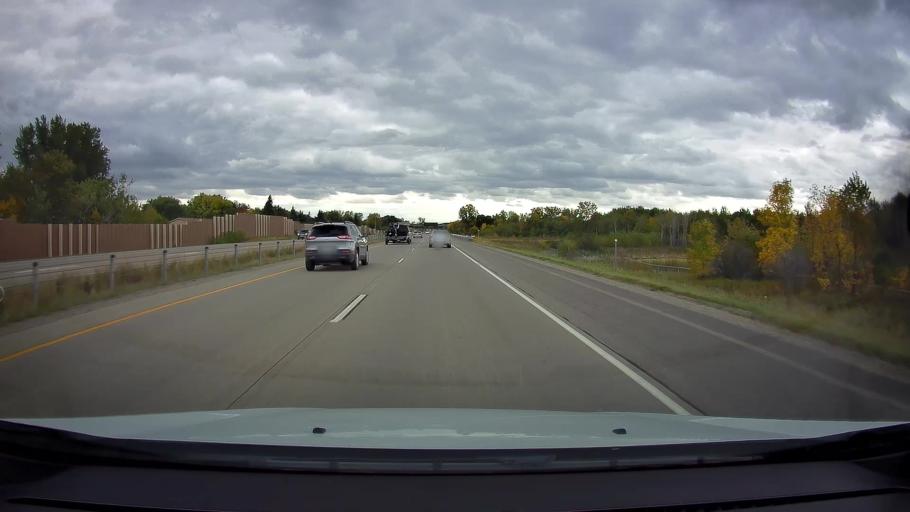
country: US
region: Minnesota
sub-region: Ramsey County
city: North Oaks
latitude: 45.1144
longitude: -93.0496
